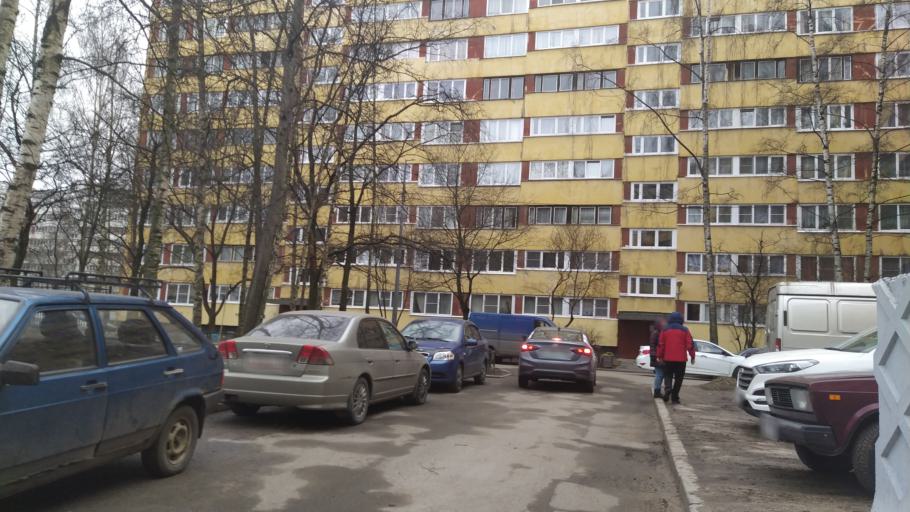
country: RU
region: St.-Petersburg
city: Komendantsky aerodrom
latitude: 60.0120
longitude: 30.2813
